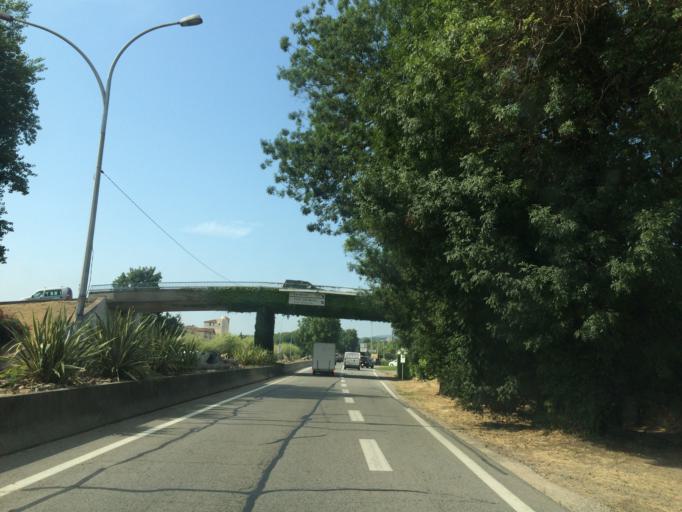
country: FR
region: Provence-Alpes-Cote d'Azur
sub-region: Departement du Var
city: Gassin
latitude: 43.2744
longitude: 6.5745
